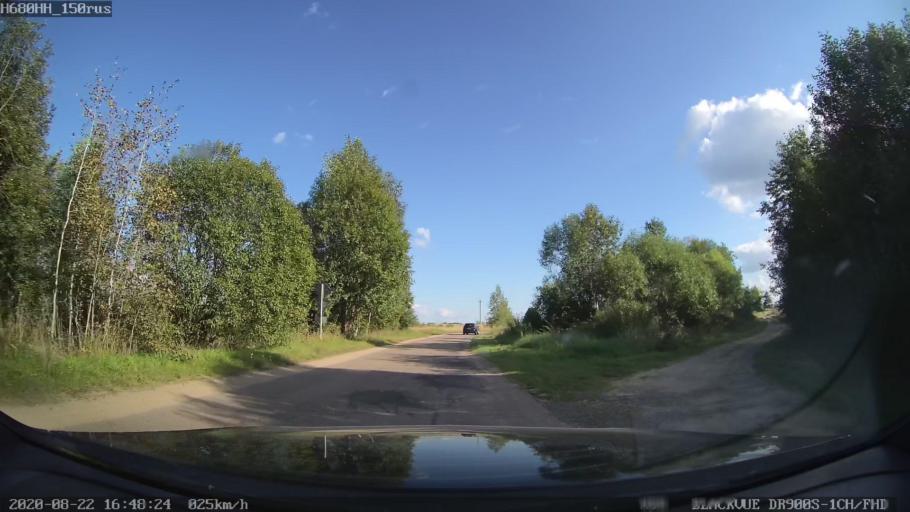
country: RU
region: Tverskaya
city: Rameshki
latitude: 57.2856
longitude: 36.0907
